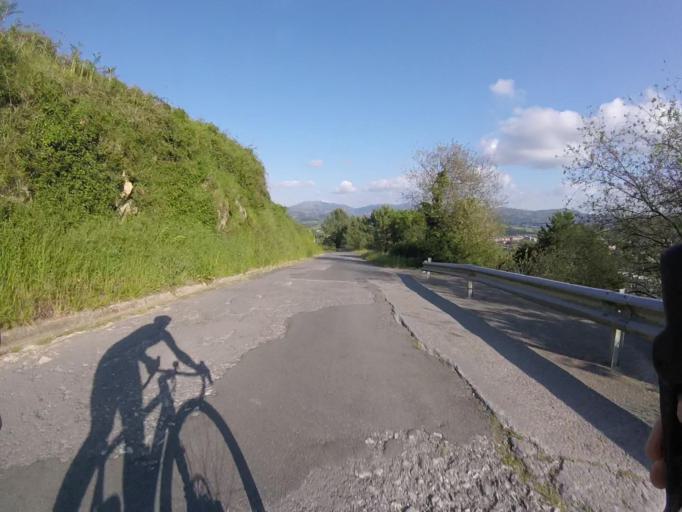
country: ES
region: Basque Country
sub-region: Provincia de Guipuzcoa
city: Pasaia
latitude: 43.3265
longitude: -1.9152
